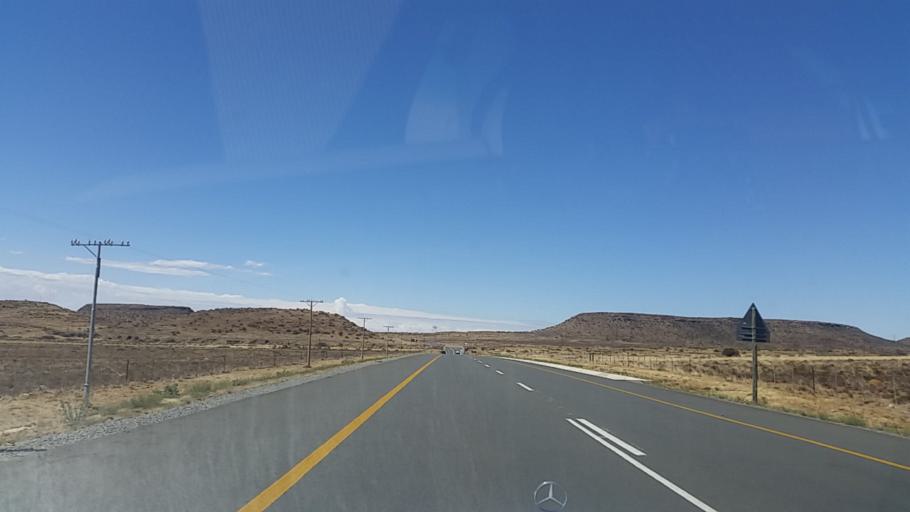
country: ZA
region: Eastern Cape
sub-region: Chris Hani District Municipality
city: Middelburg
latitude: -31.3661
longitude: 25.0194
